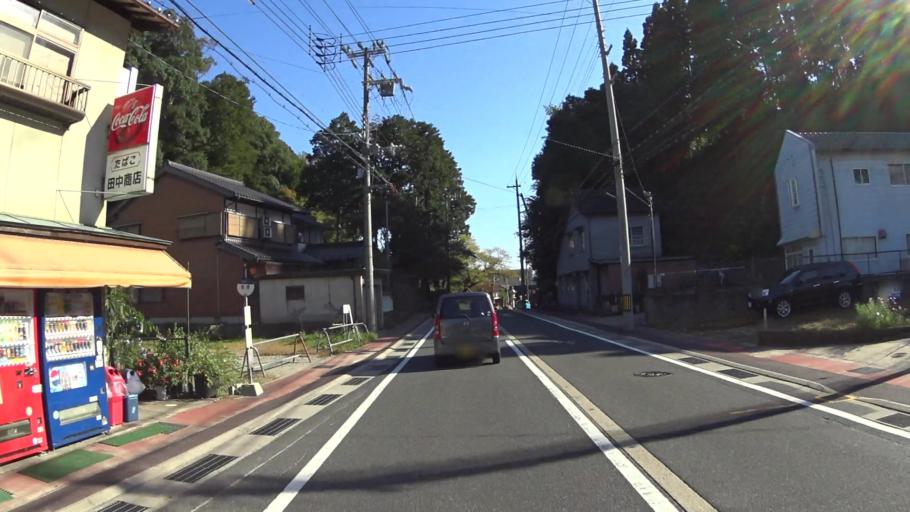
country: JP
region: Kyoto
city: Miyazu
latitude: 35.6313
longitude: 135.0548
